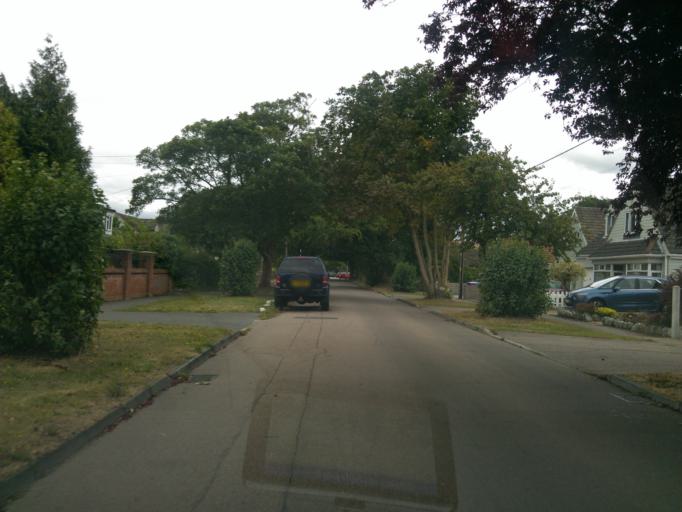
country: GB
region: England
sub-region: Essex
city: West Mersea
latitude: 51.7807
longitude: 0.9285
